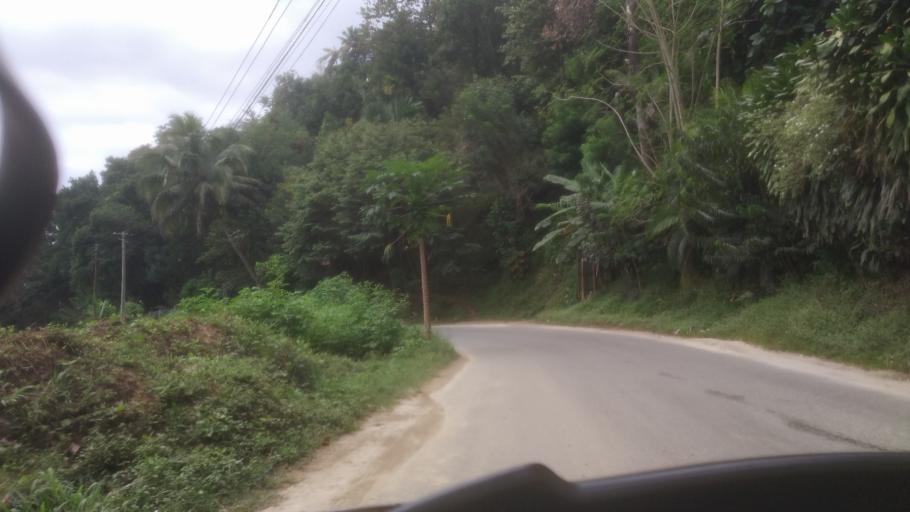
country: IN
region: Kerala
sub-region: Idukki
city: Munnar
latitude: 9.9802
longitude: 77.0004
